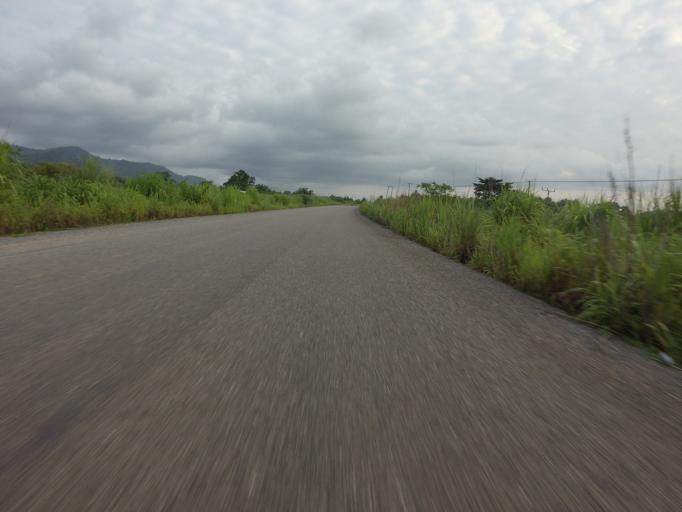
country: GH
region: Volta
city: Kpandu
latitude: 6.8436
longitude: 0.3898
